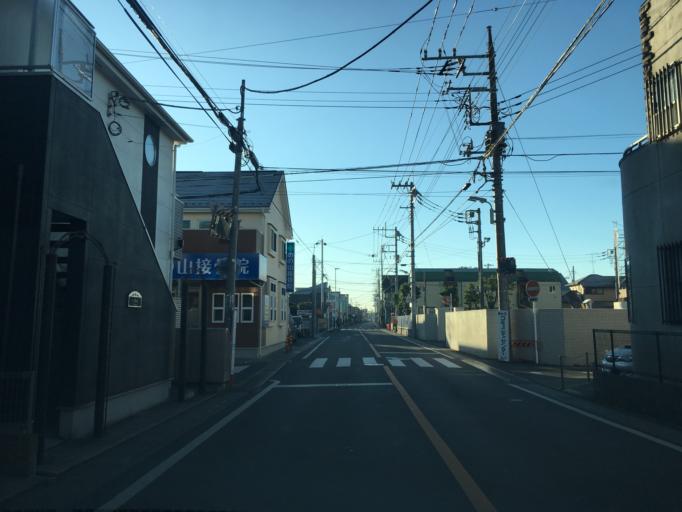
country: JP
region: Saitama
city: Sayama
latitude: 35.8083
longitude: 139.4170
